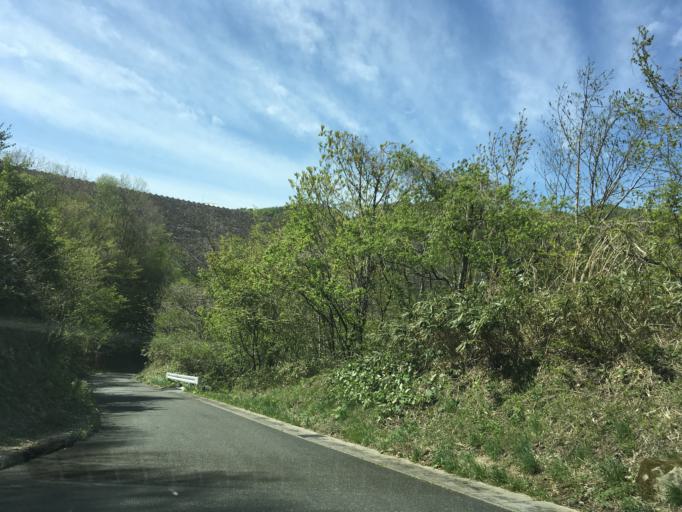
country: JP
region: Iwate
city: Mizusawa
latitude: 39.1195
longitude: 140.9237
